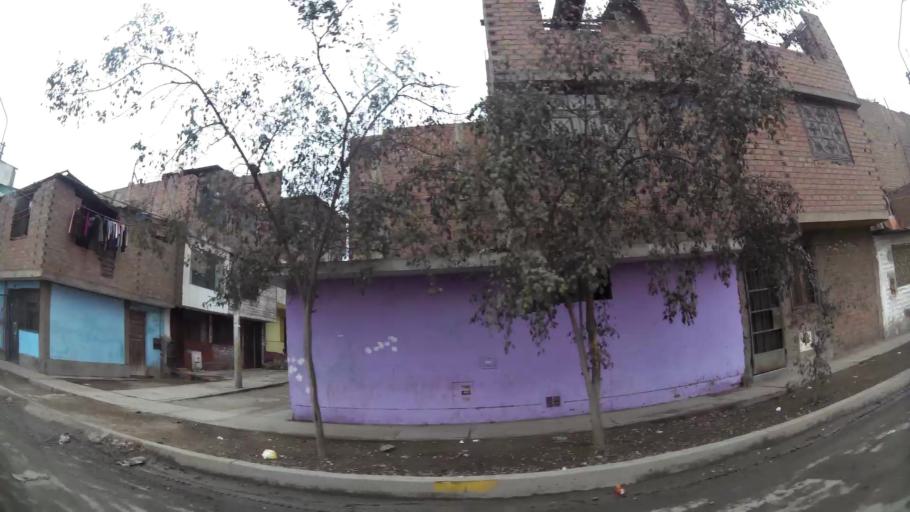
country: PE
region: Lima
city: Lima
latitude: -12.0352
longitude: -77.0077
